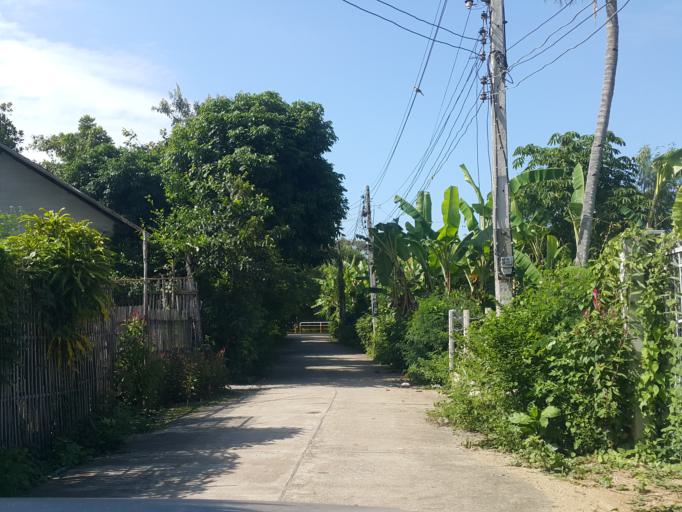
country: TH
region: Chiang Mai
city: Saraphi
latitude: 18.7302
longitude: 99.0431
